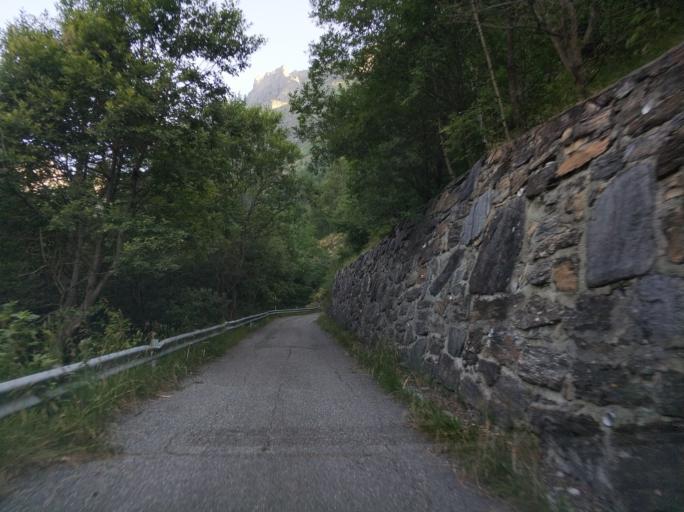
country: IT
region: Piedmont
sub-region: Provincia di Torino
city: Usseglio
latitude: 45.2350
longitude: 7.2024
